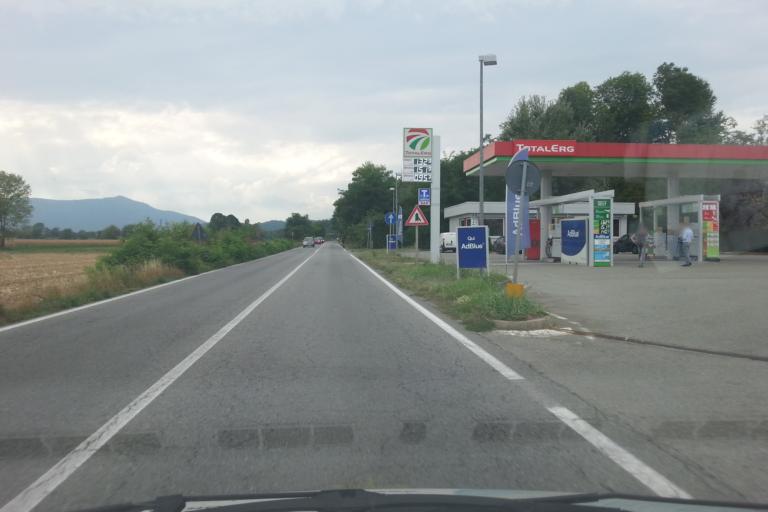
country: IT
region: Piedmont
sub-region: Provincia di Torino
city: Pasta
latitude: 45.0281
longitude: 7.5420
